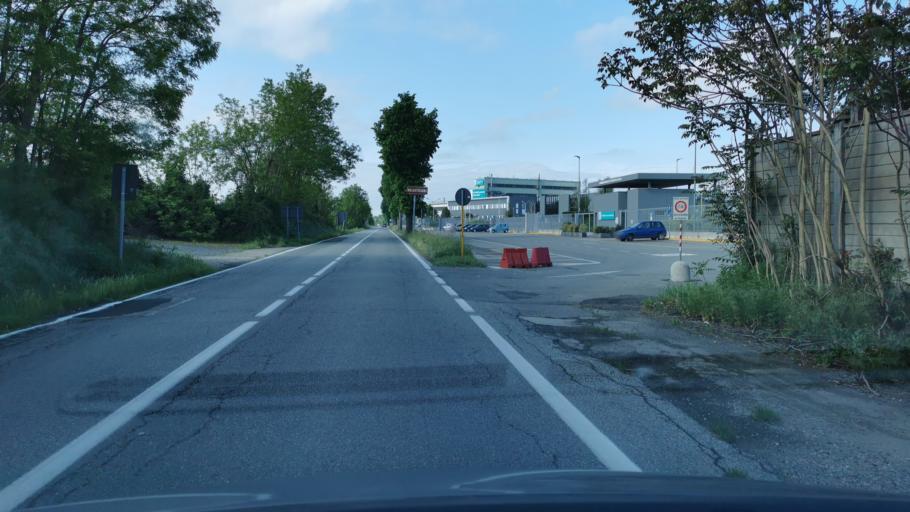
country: IT
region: Piedmont
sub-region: Provincia di Torino
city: Santena
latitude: 44.9344
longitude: 7.7586
